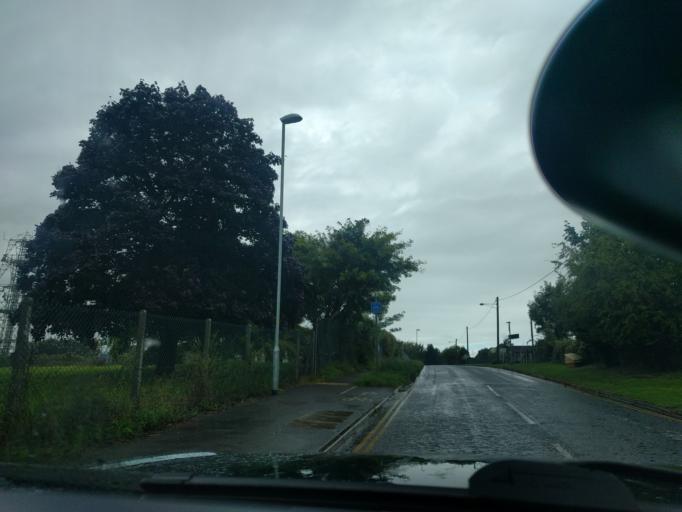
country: GB
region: England
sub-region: Wiltshire
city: Neston
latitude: 51.4227
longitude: -2.2221
